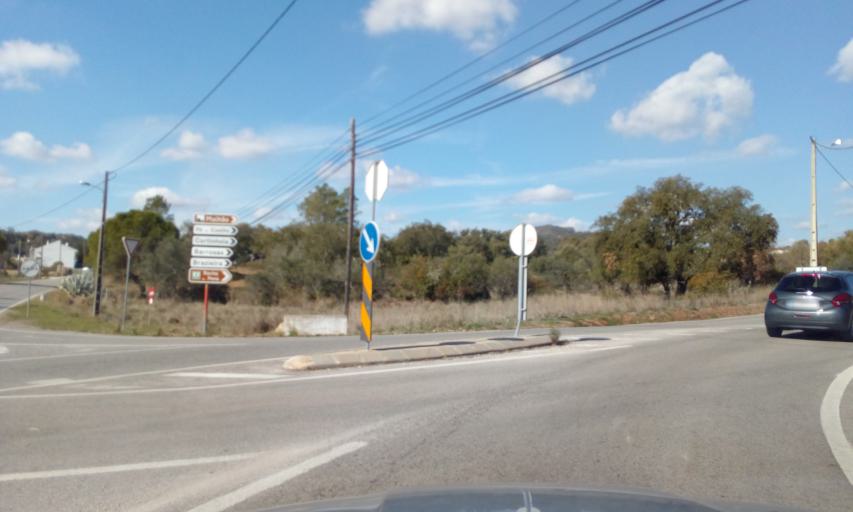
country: PT
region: Faro
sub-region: Loule
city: Loule
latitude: 37.2432
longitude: -8.0605
